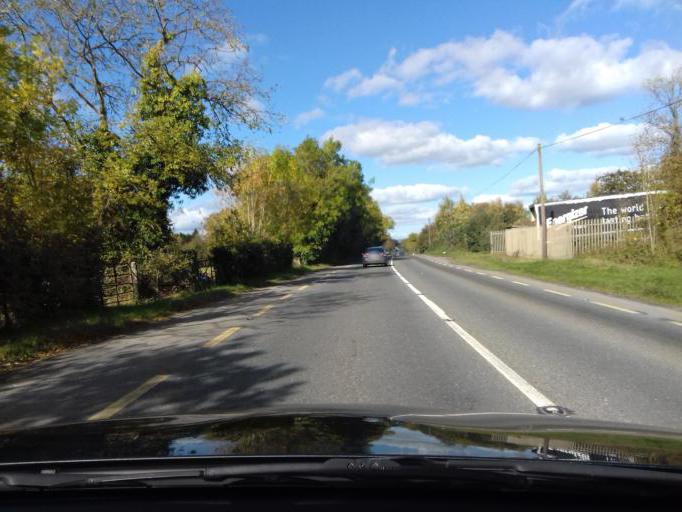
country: IE
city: Kentstown
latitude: 53.6559
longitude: -6.5222
